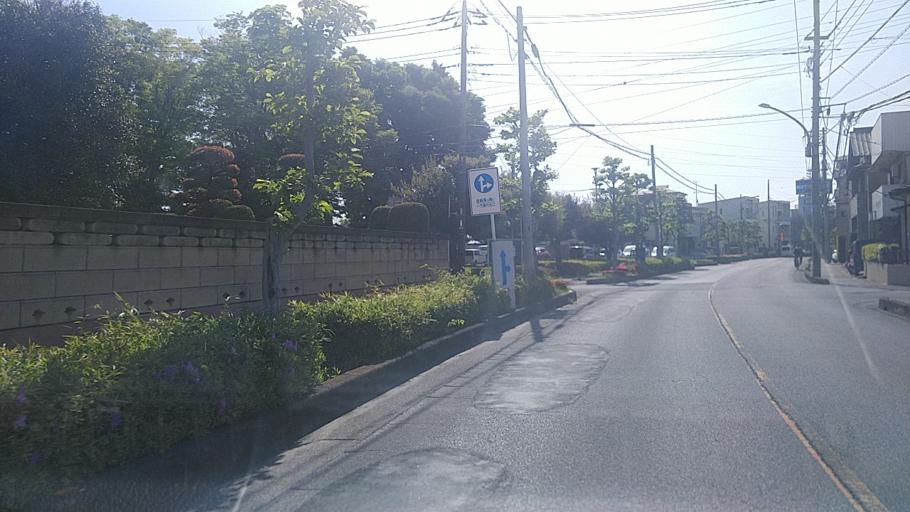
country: JP
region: Saitama
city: Koshigaya
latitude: 35.8771
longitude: 139.7553
